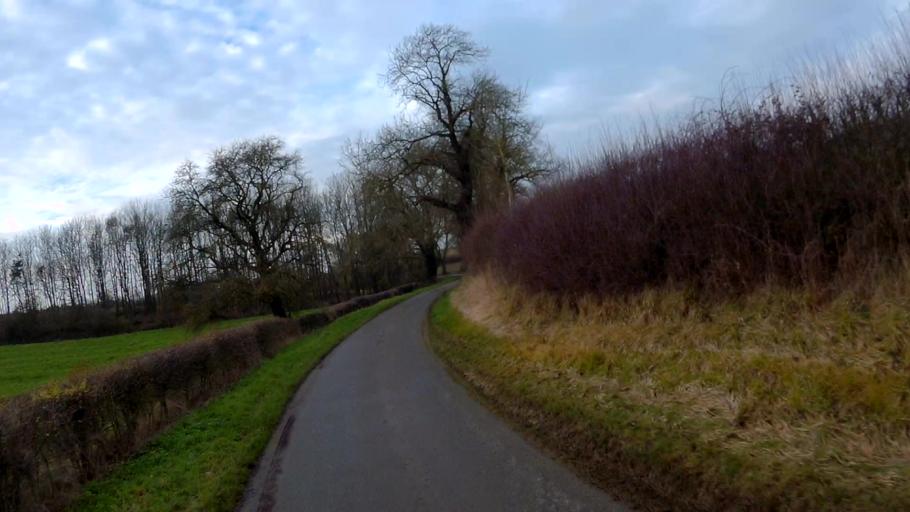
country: GB
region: England
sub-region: Lincolnshire
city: Bourne
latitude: 52.8290
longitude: -0.4699
